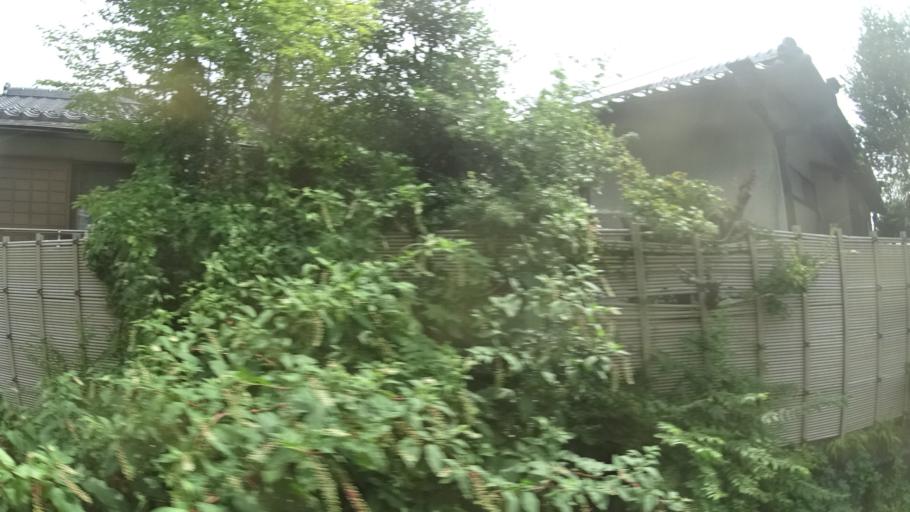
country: JP
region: Tochigi
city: Imaichi
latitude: 36.7150
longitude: 139.6963
